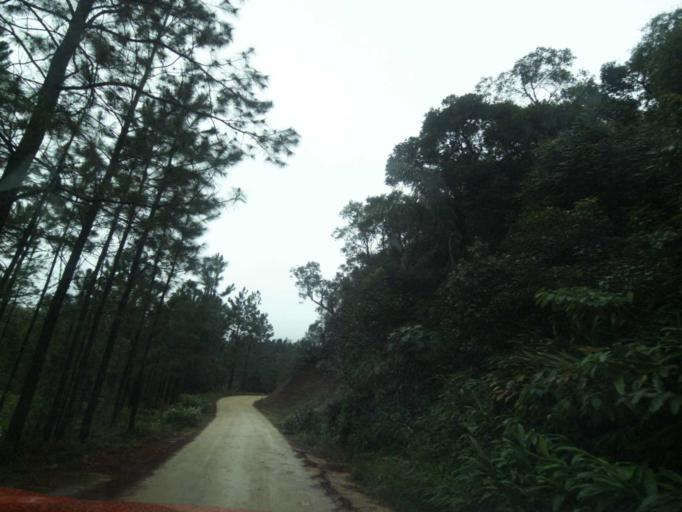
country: BR
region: Santa Catarina
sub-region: Anitapolis
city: Anitapolis
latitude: -27.9221
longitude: -49.1855
